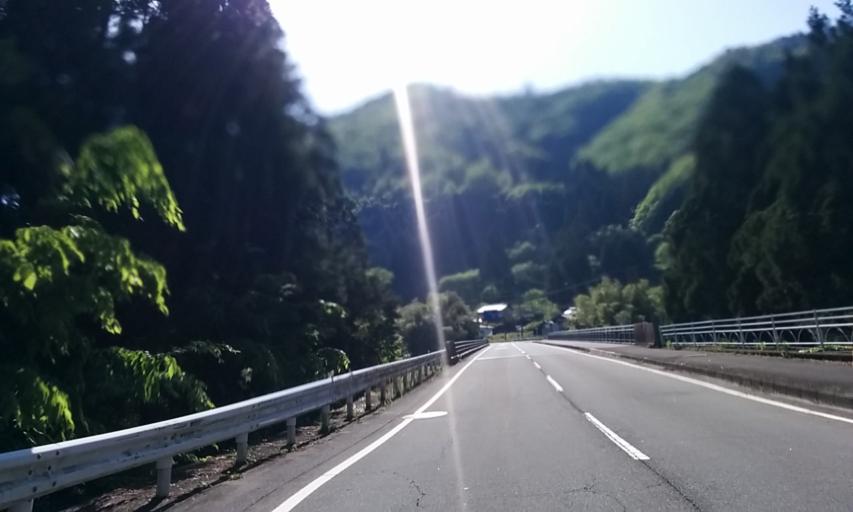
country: JP
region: Kyoto
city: Ayabe
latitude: 35.2641
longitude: 135.4320
